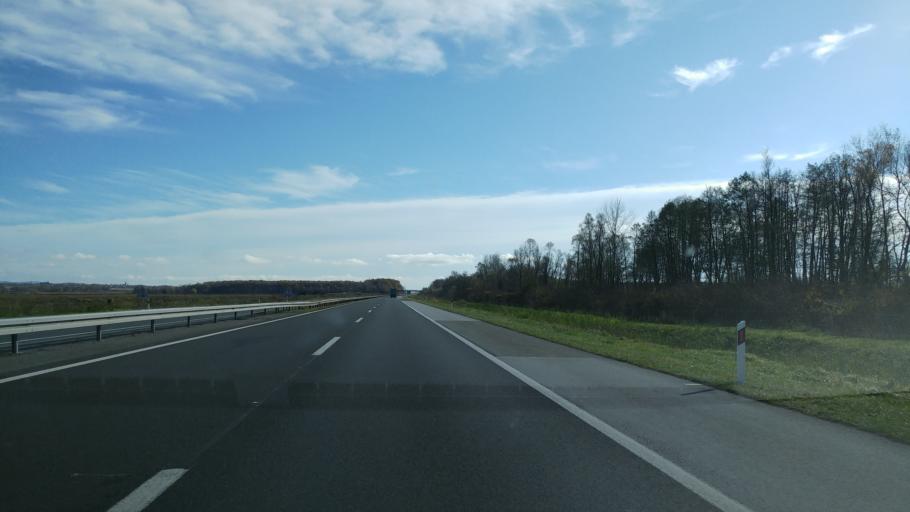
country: HR
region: Sisacko-Moslavacka
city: Lipovljani
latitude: 45.4202
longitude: 16.8448
